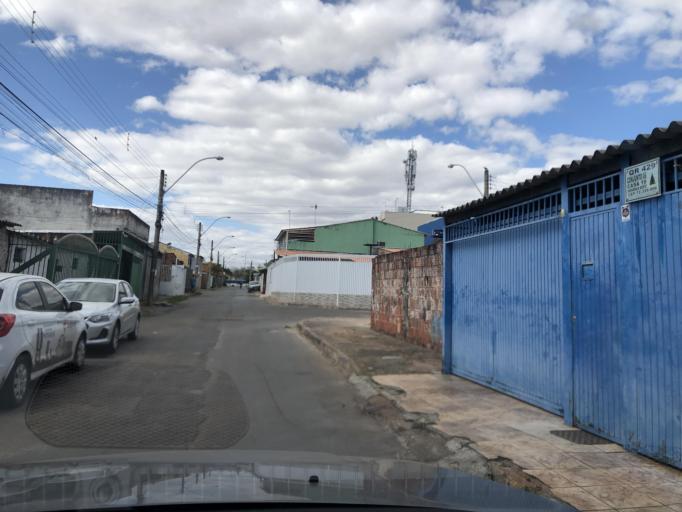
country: BR
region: Federal District
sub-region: Brasilia
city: Brasilia
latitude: -15.8937
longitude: -48.1414
